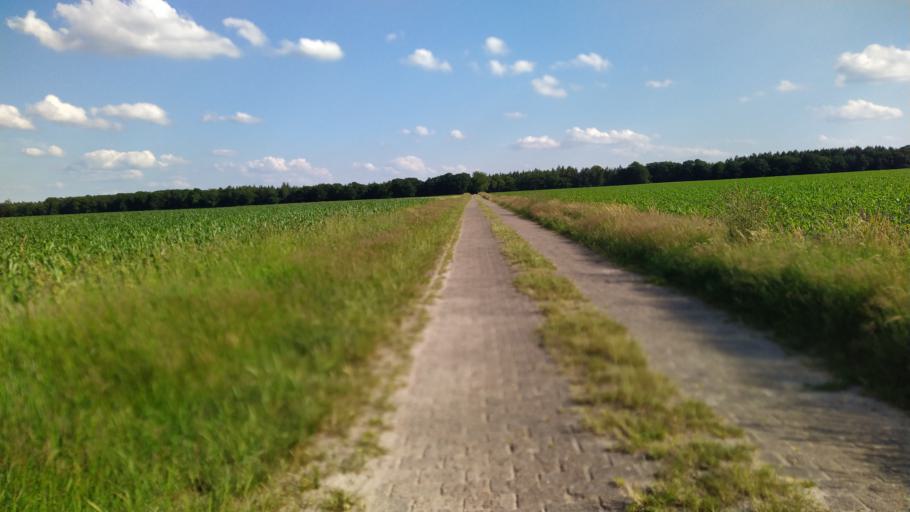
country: DE
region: Lower Saxony
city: Lintig
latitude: 53.6032
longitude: 8.8927
